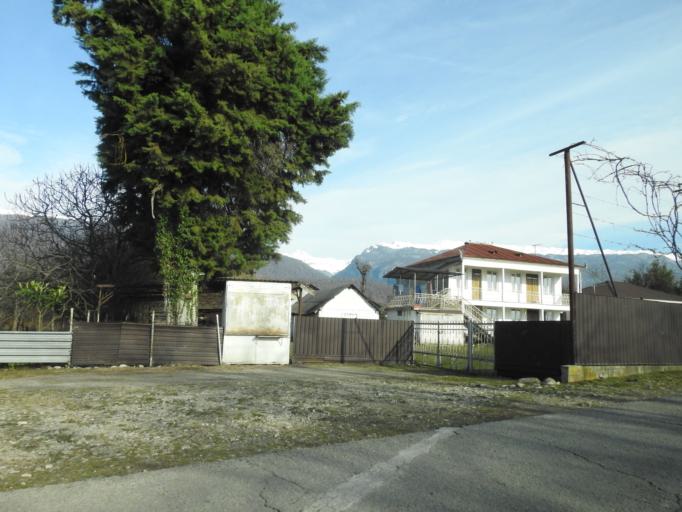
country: GE
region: Abkhazia
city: Gudauta
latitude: 43.1937
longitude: 40.6289
